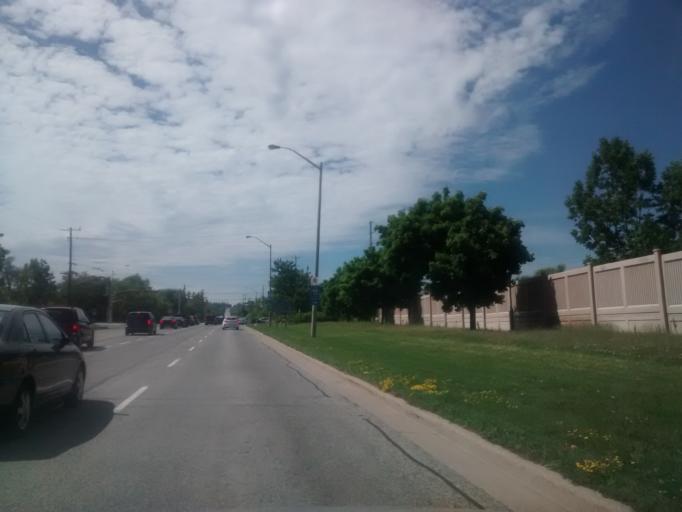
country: CA
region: Ontario
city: Burlington
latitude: 43.3768
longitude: -79.8384
